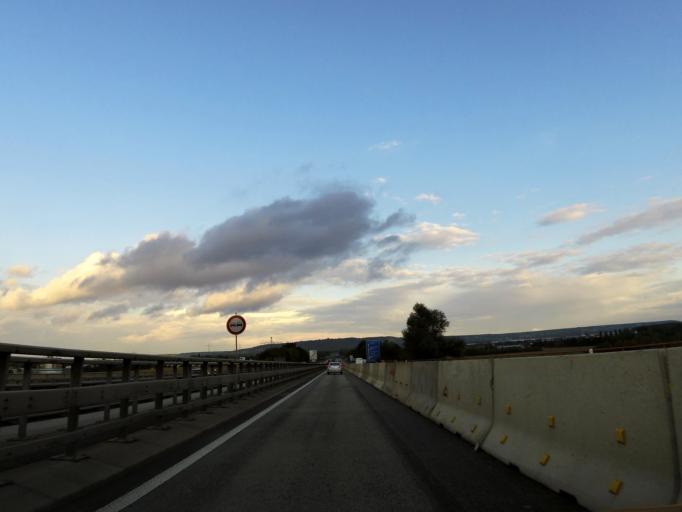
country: DE
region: Rheinland-Pfalz
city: Laubenheim
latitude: 49.9329
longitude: 7.8992
